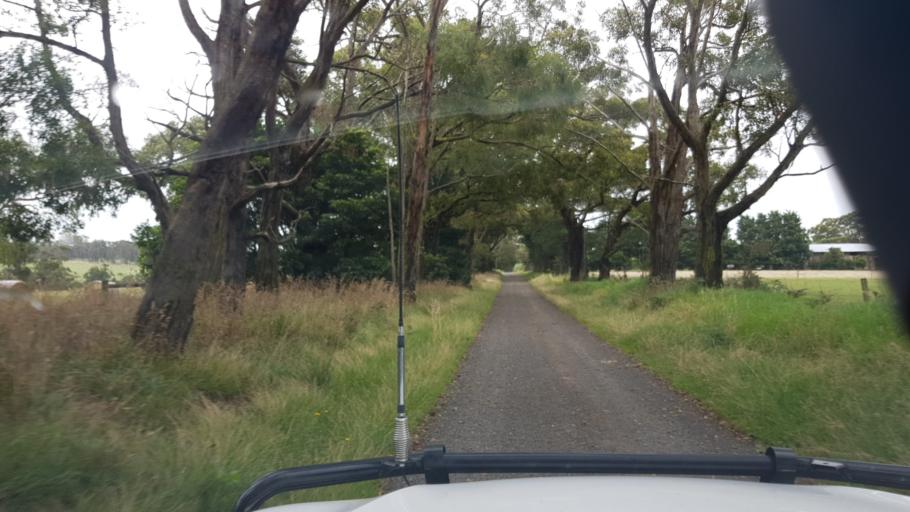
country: AU
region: Victoria
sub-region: Cardinia
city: Bunyip
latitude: -38.1547
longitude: 145.7980
